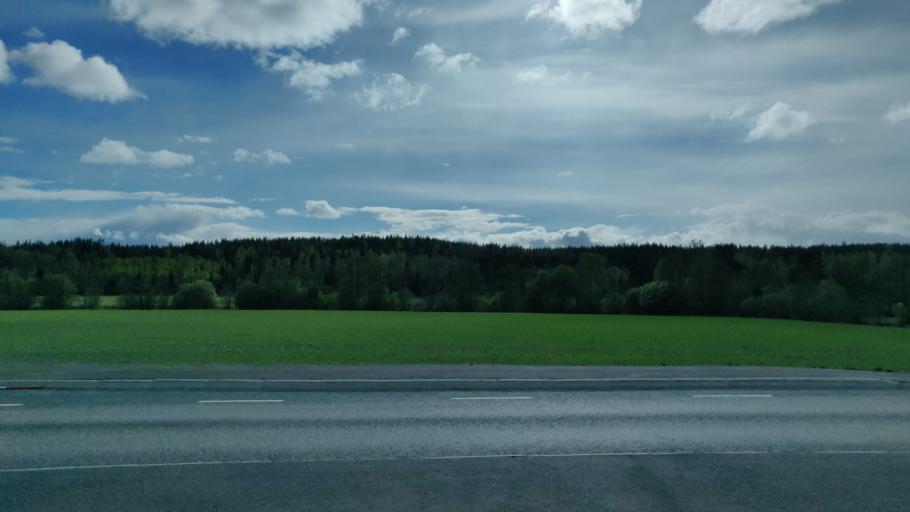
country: SE
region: Vaermland
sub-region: Forshaga Kommun
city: Deje
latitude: 59.5651
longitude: 13.4795
